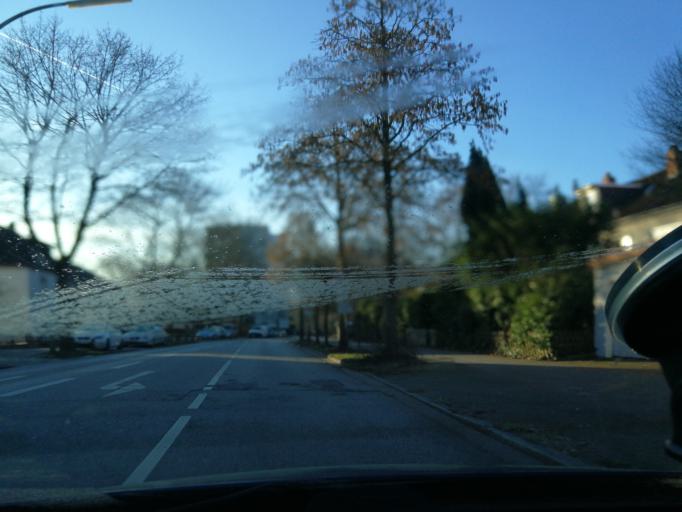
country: DE
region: Hamburg
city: Harburg
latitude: 53.4620
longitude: 9.9573
